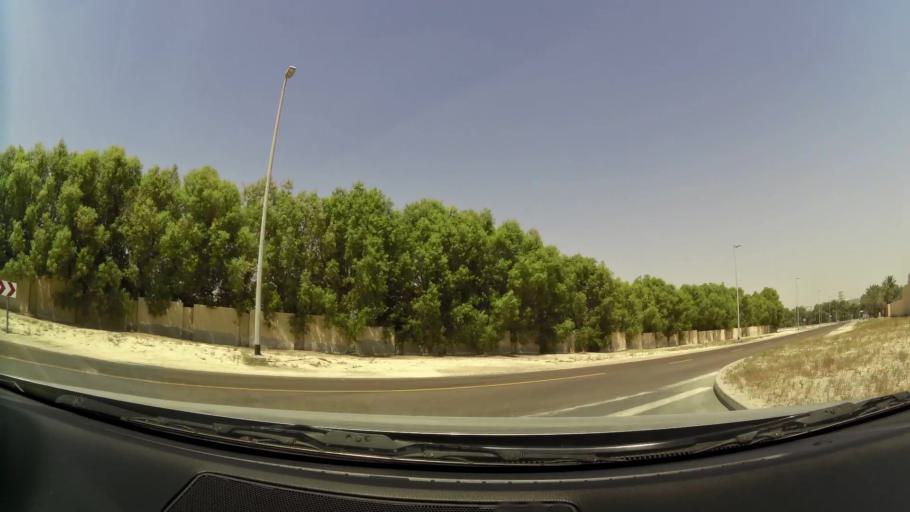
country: AE
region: Dubai
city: Dubai
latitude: 25.1277
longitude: 55.1852
